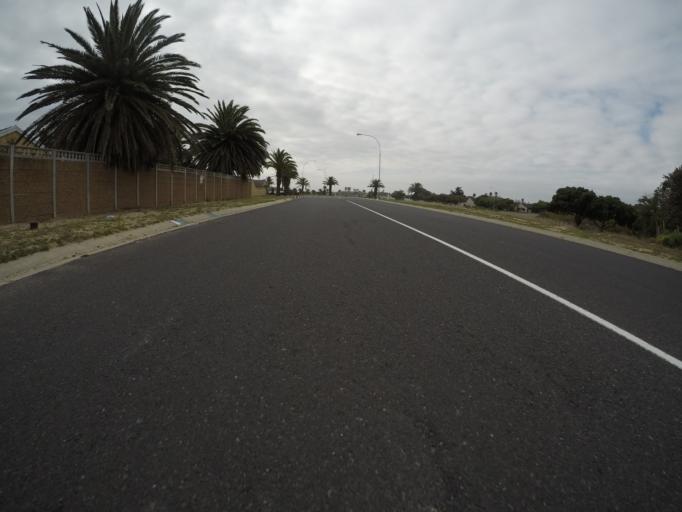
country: ZA
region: Western Cape
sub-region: City of Cape Town
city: Atlantis
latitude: -33.6958
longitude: 18.4441
